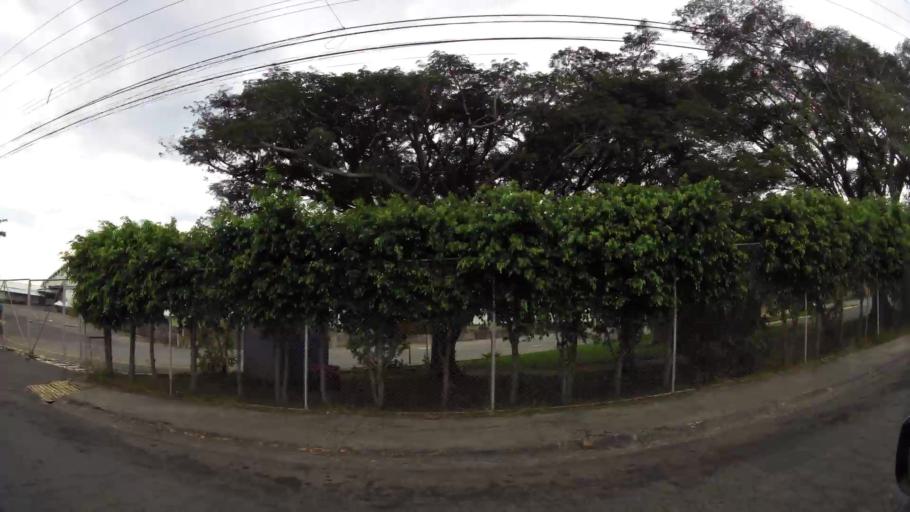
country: CR
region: Heredia
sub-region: Canton de Belen
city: San Antonio
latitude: 9.9671
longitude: -84.1899
